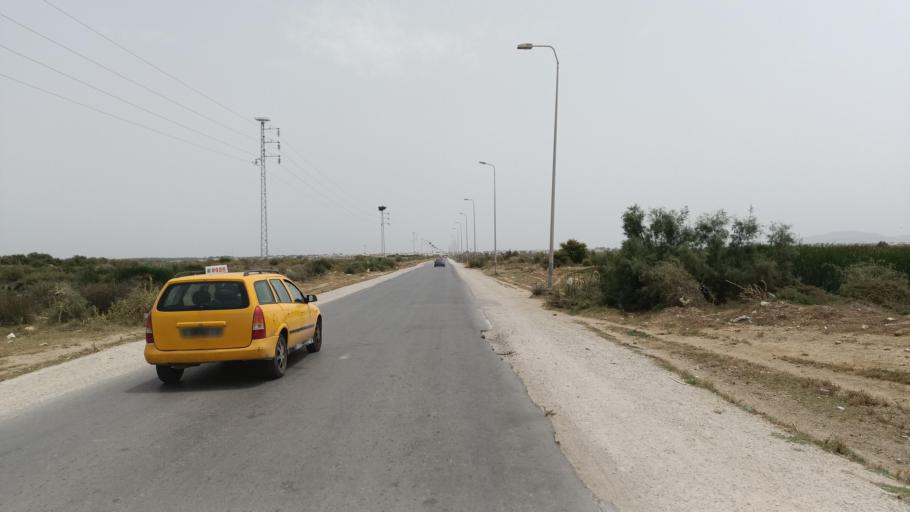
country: TN
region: Nabul
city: Manzil Bu Zalafah
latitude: 36.7236
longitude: 10.4721
